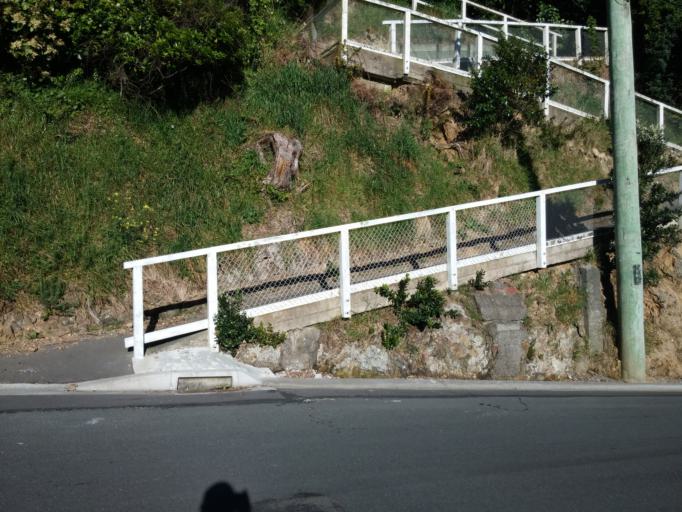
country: NZ
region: Wellington
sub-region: Wellington City
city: Kelburn
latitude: -41.2767
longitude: 174.7574
